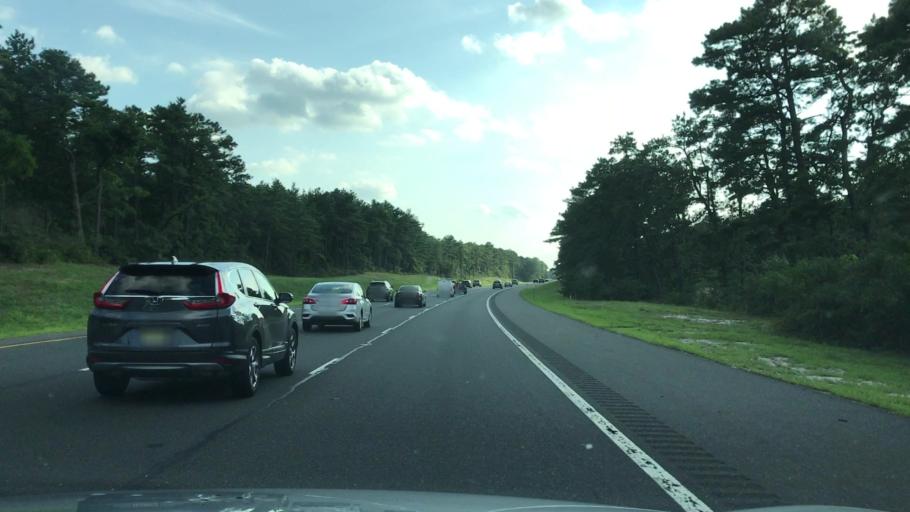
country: US
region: New Jersey
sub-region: Ocean County
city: Tuckerton
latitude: 39.6381
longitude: -74.3722
